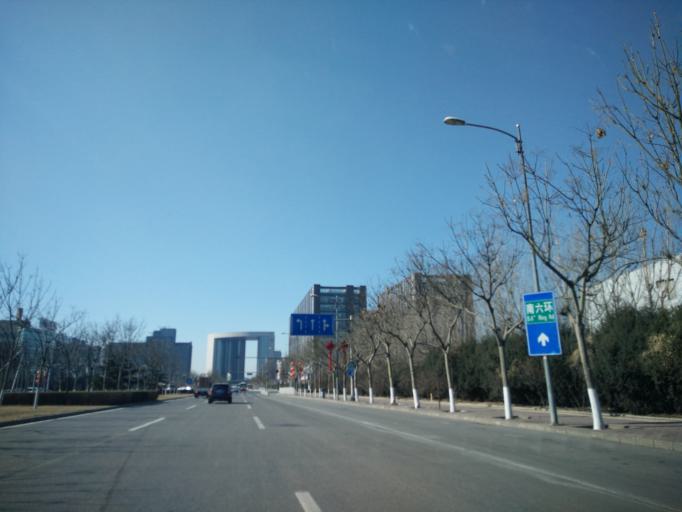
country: CN
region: Beijing
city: Jiugong
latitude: 39.7837
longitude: 116.5223
